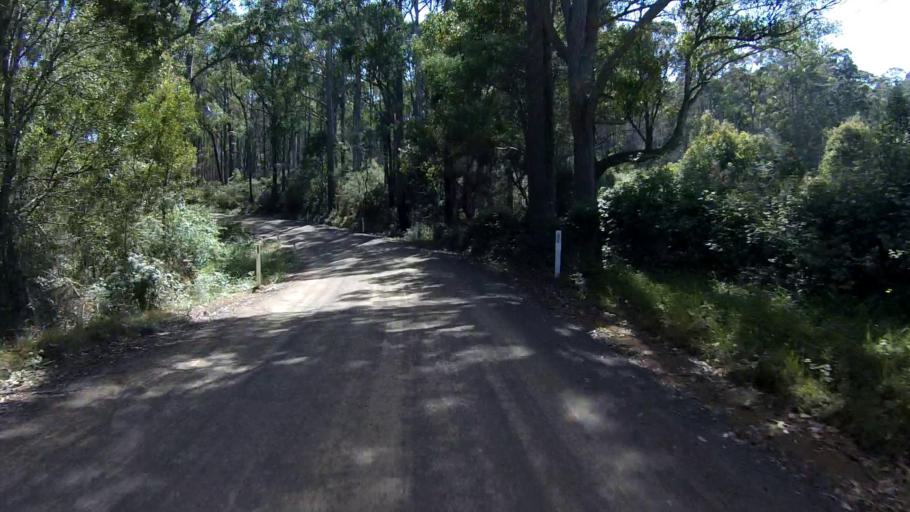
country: AU
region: Tasmania
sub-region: Sorell
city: Sorell
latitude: -42.7023
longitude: 147.7431
